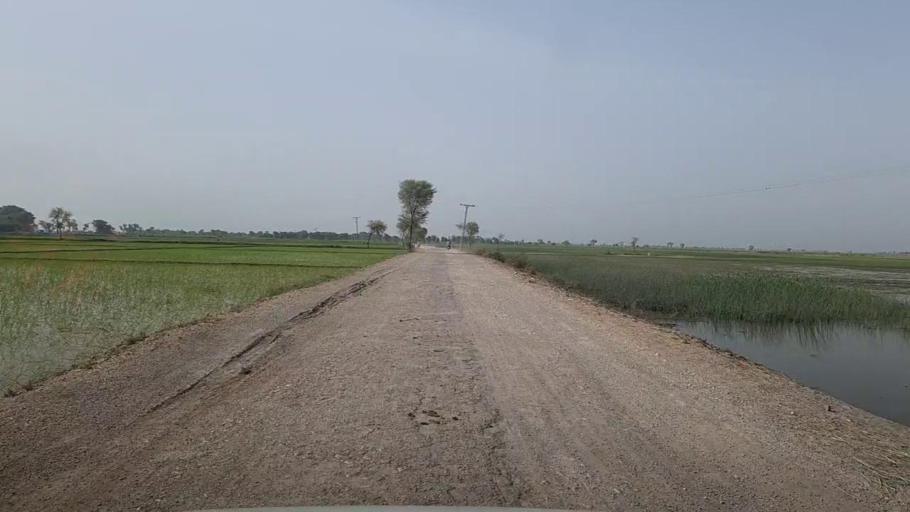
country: PK
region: Sindh
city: Mehar
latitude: 27.1116
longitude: 67.8199
